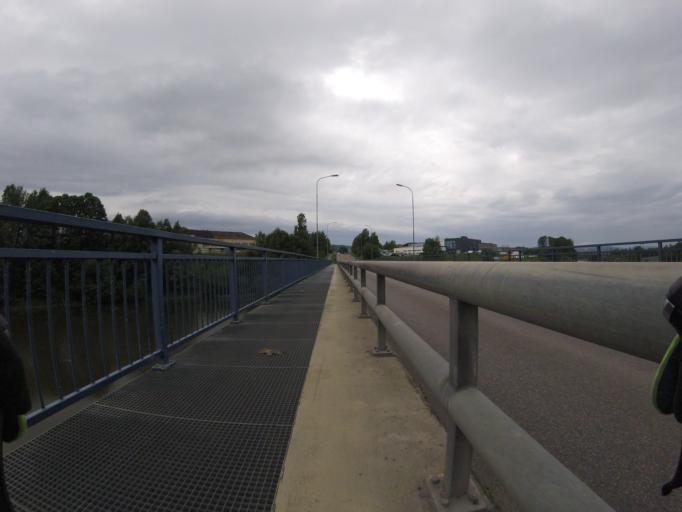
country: NO
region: Akershus
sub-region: Skedsmo
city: Lillestrom
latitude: 59.9797
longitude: 11.0081
